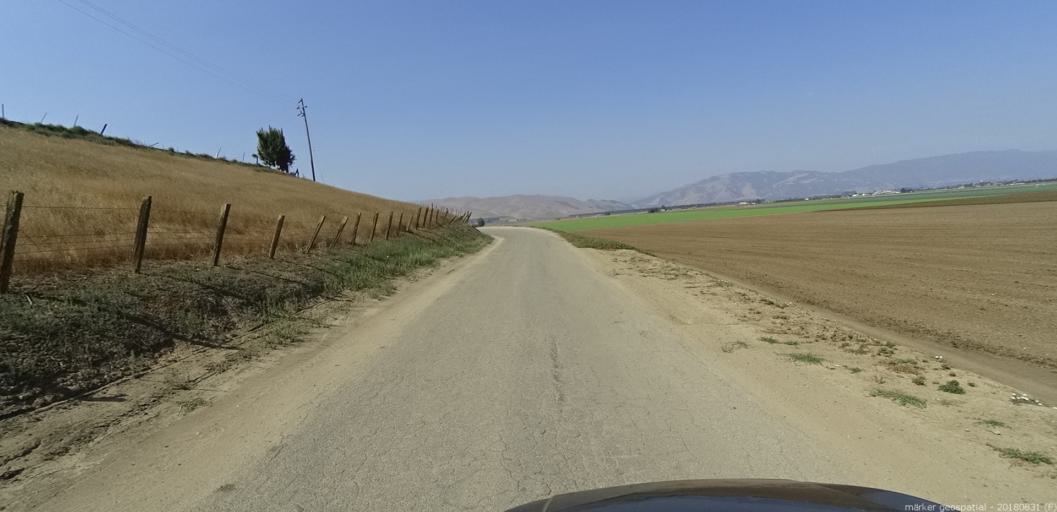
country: US
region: California
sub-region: Monterey County
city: Greenfield
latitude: 36.3061
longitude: -121.2046
